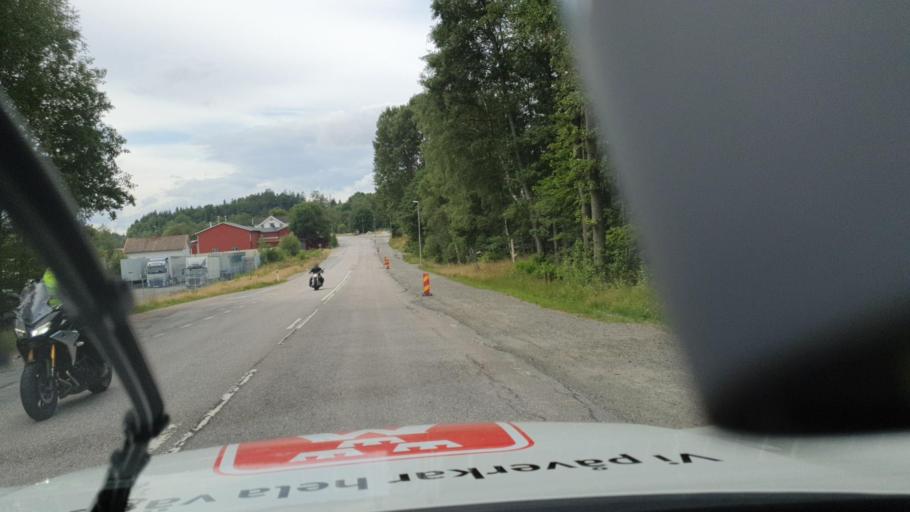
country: SE
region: Vaestra Goetaland
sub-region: Harryda Kommun
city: Landvetter
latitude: 57.6916
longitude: 12.2868
